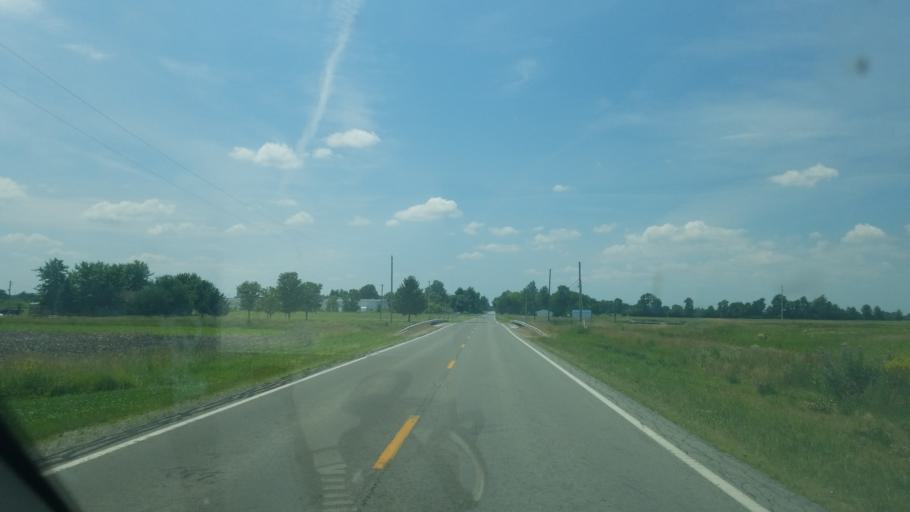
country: US
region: Ohio
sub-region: Hardin County
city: Ada
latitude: 40.7766
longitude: -83.8020
